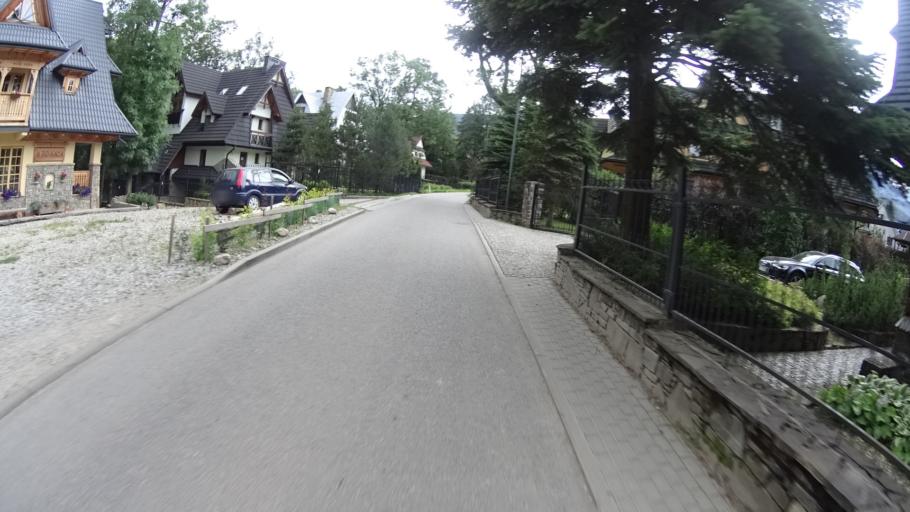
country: PL
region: Lesser Poland Voivodeship
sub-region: Powiat tatrzanski
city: Zakopane
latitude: 49.2871
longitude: 19.9519
